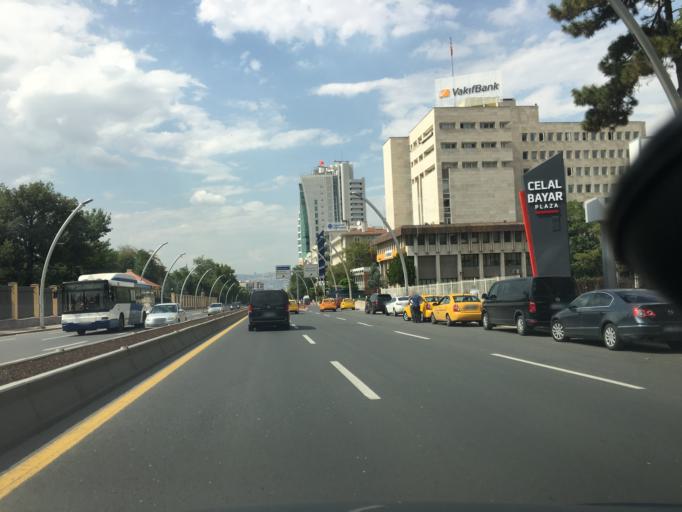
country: TR
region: Ankara
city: Cankaya
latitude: 39.9057
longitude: 32.8580
